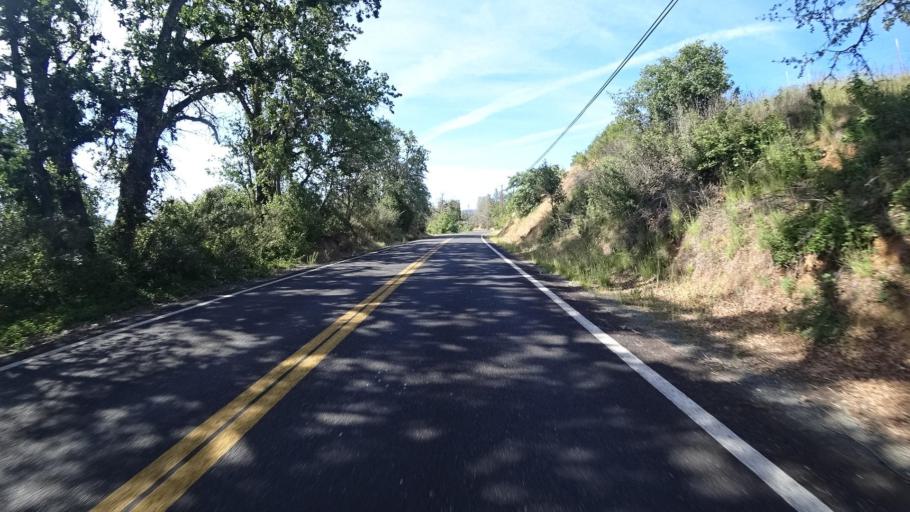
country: US
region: California
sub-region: Lake County
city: Kelseyville
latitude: 38.9648
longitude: -122.8980
